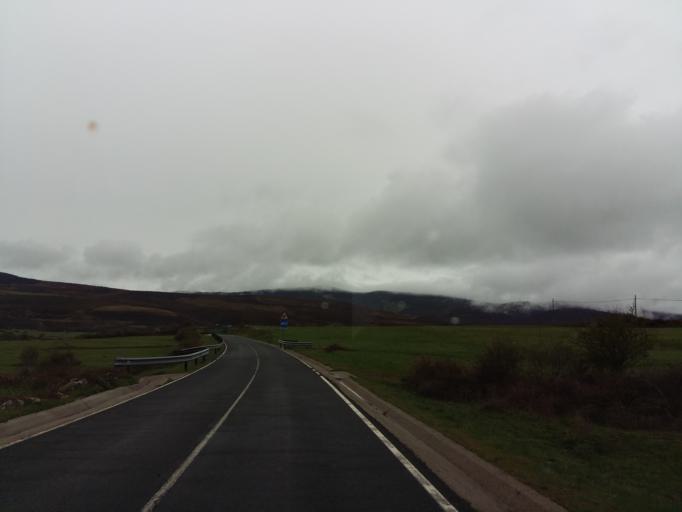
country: ES
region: Cantabria
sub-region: Provincia de Cantabria
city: Villaescusa
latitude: 42.9358
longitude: -4.1976
